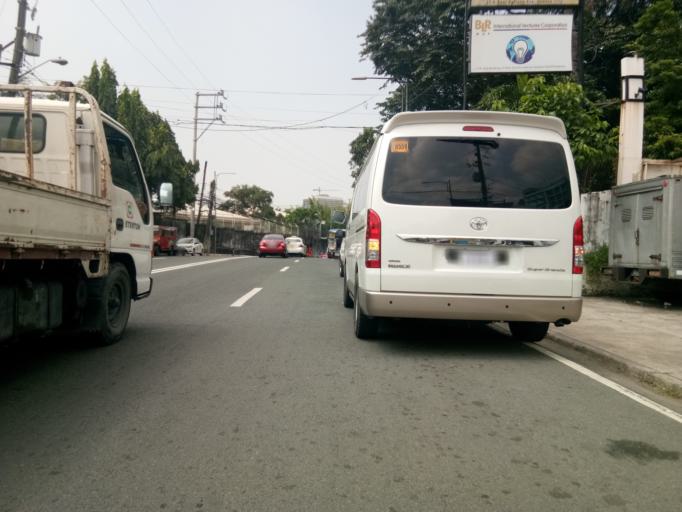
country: PH
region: Metro Manila
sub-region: San Juan
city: San Juan
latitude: 14.6089
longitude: 121.0446
